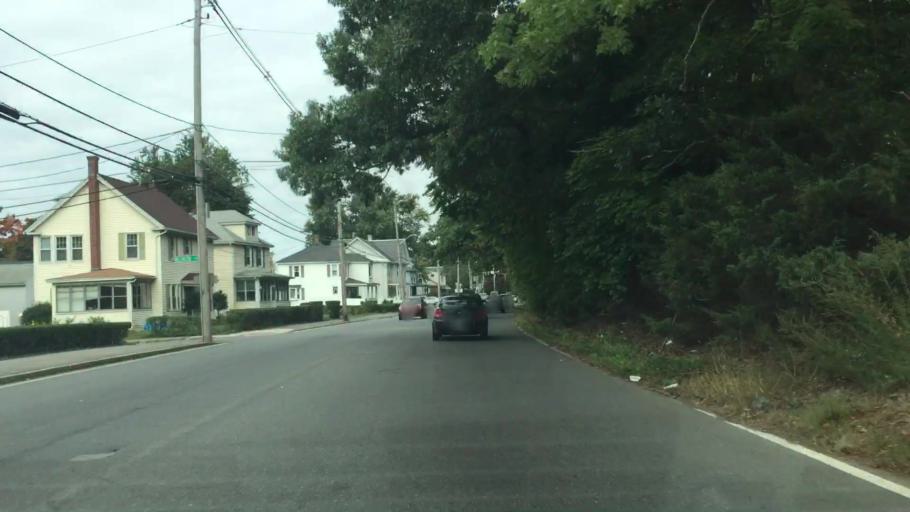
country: US
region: Massachusetts
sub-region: Middlesex County
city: Lowell
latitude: 42.6340
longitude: -71.2909
